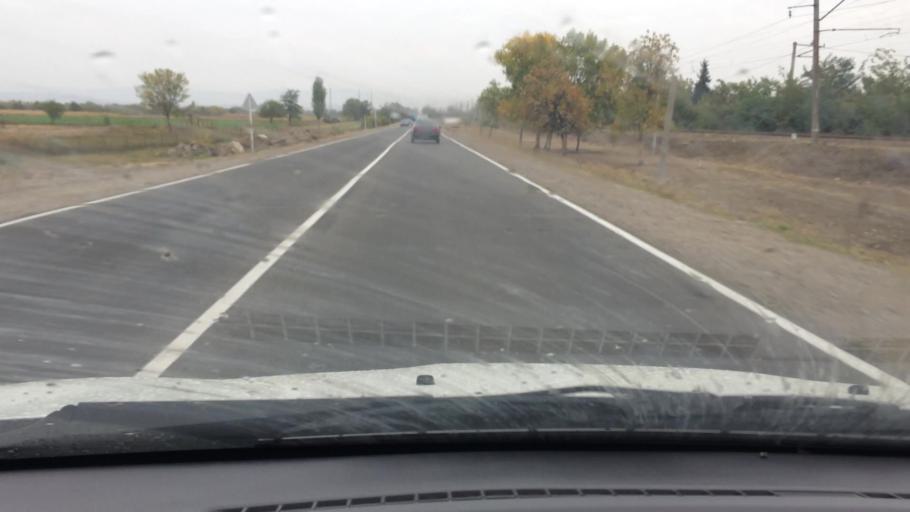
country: GE
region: Kvemo Kartli
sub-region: Marneuli
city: Marneuli
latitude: 41.4228
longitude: 44.8242
